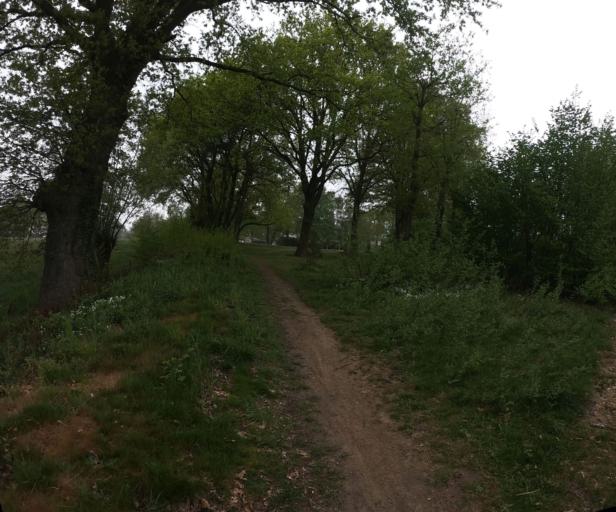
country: BE
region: Flanders
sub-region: Provincie Vlaams-Brabant
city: Gooik
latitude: 50.7743
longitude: 4.1057
